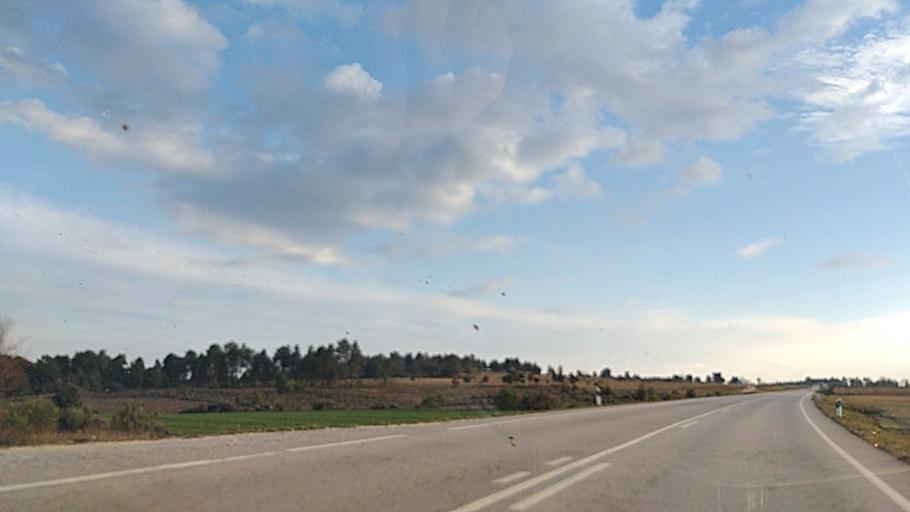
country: PT
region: Guarda
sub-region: Pinhel
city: Pinhel
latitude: 40.6548
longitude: -6.9666
